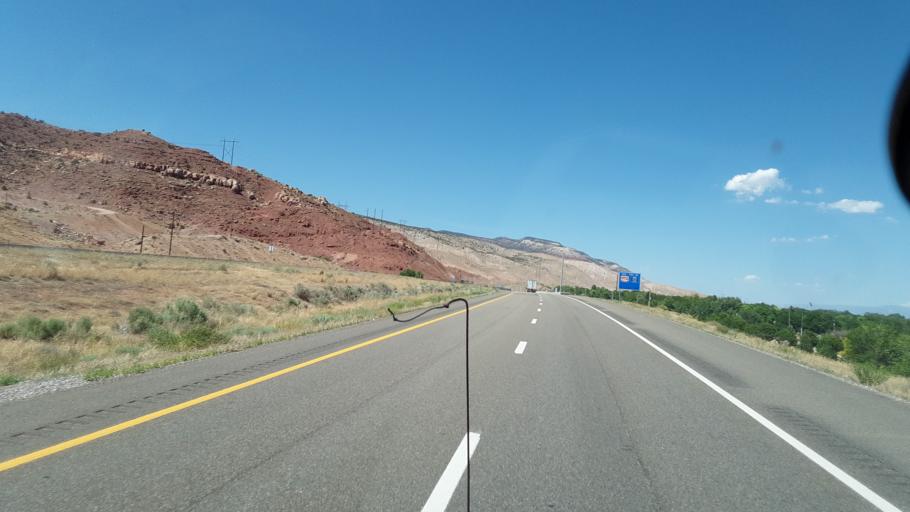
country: US
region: Utah
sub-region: Sevier County
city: Richfield
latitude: 38.7768
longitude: -112.0962
